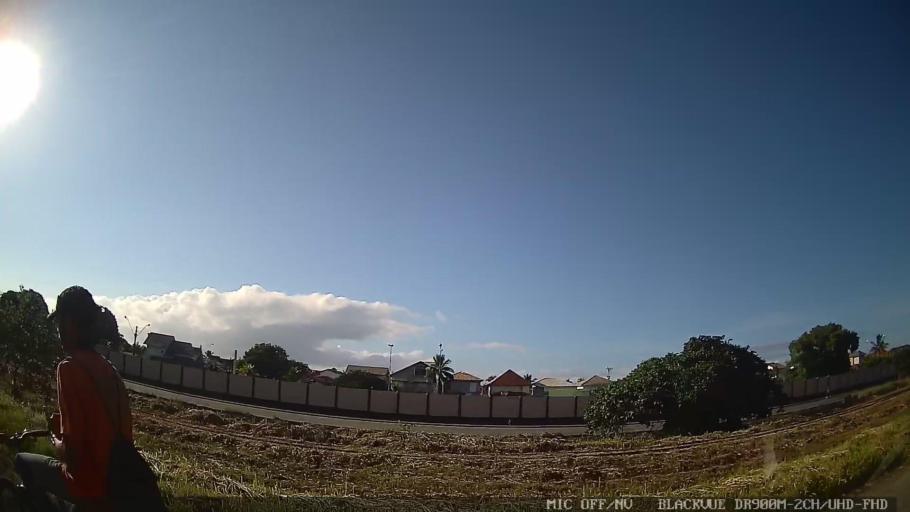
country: BR
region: Sao Paulo
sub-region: Peruibe
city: Peruibe
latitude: -24.2790
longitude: -46.9575
